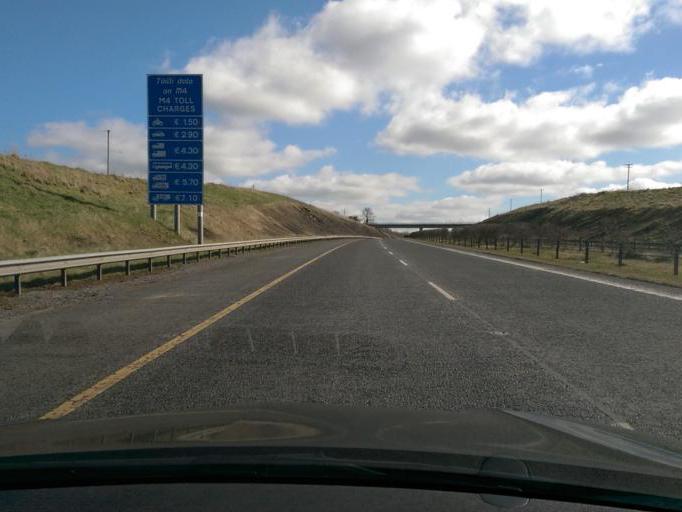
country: IE
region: Leinster
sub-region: An Mhi
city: Enfield
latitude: 53.4123
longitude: -6.7602
